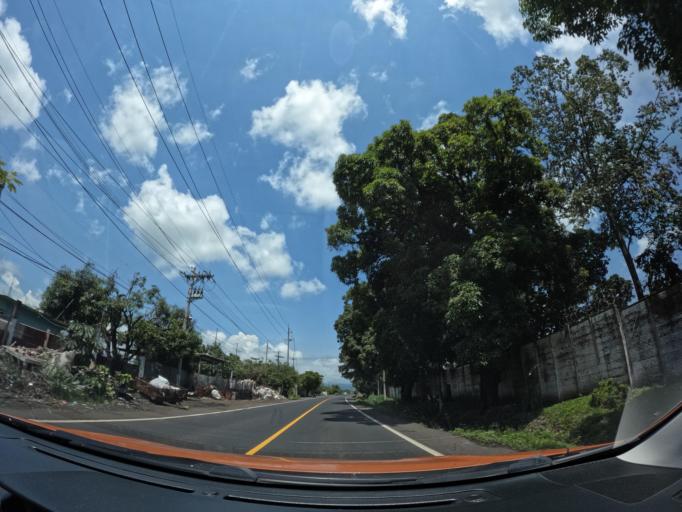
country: GT
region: Escuintla
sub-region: Municipio de Masagua
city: Masagua
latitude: 14.2365
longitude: -90.8199
